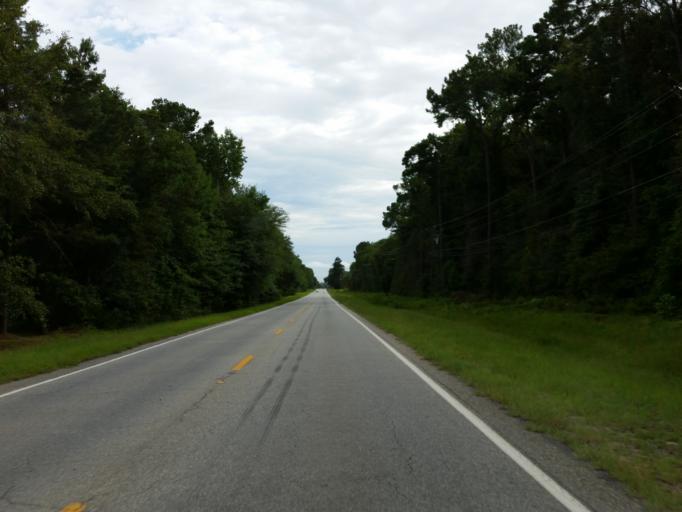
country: US
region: Georgia
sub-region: Lowndes County
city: Valdosta
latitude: 30.7166
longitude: -83.2961
